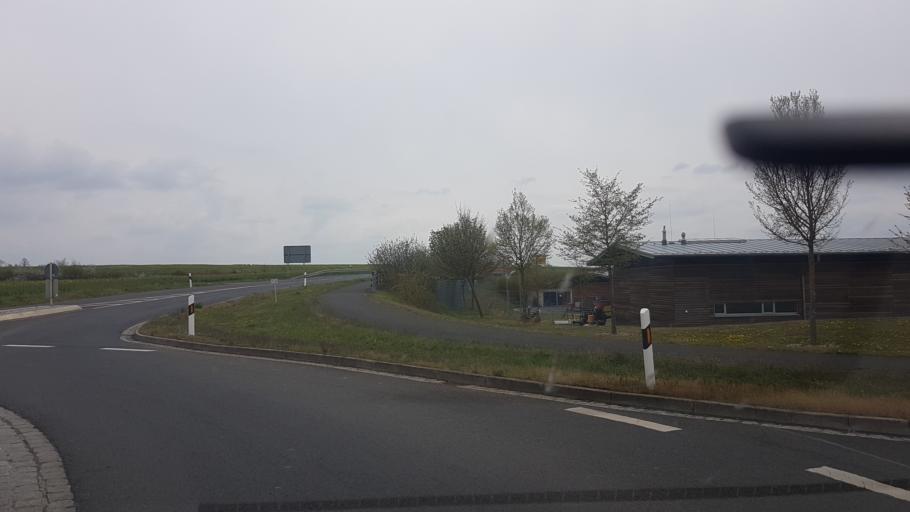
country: DE
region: Bavaria
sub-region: Regierungsbezirk Unterfranken
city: Rodelmaier
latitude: 50.3262
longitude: 10.2673
